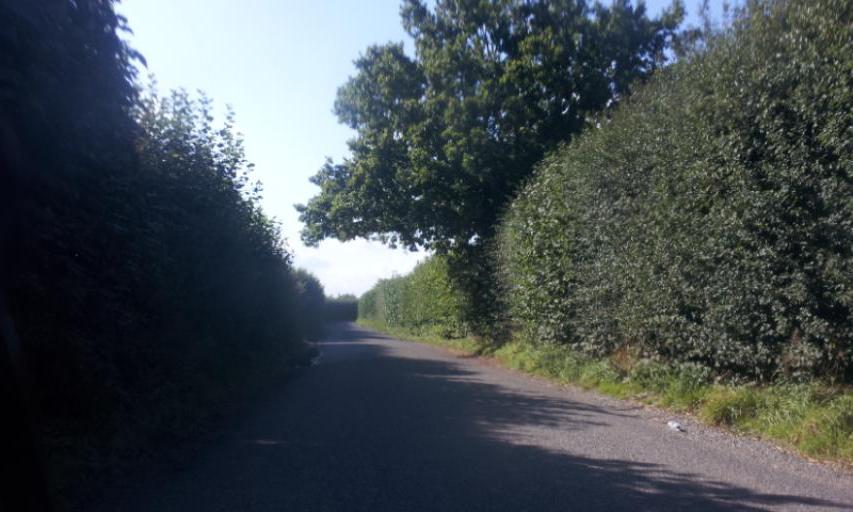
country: GB
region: England
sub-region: Kent
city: Hadlow
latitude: 51.2206
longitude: 0.3535
